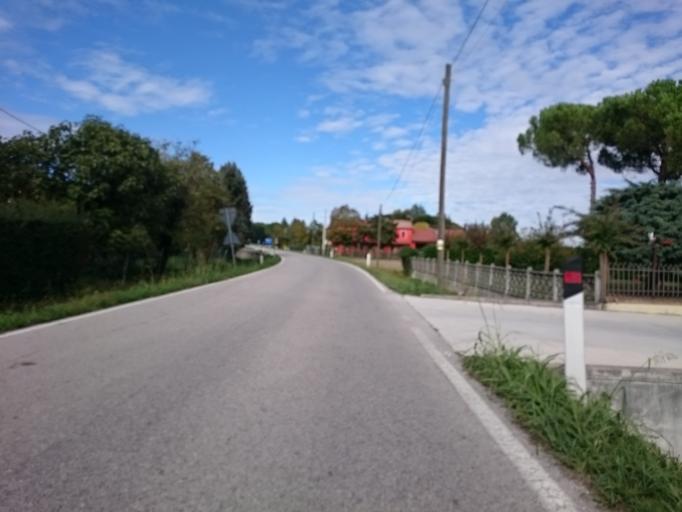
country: IT
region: Veneto
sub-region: Provincia di Padova
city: Bovolenta
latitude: 45.2644
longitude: 11.9409
